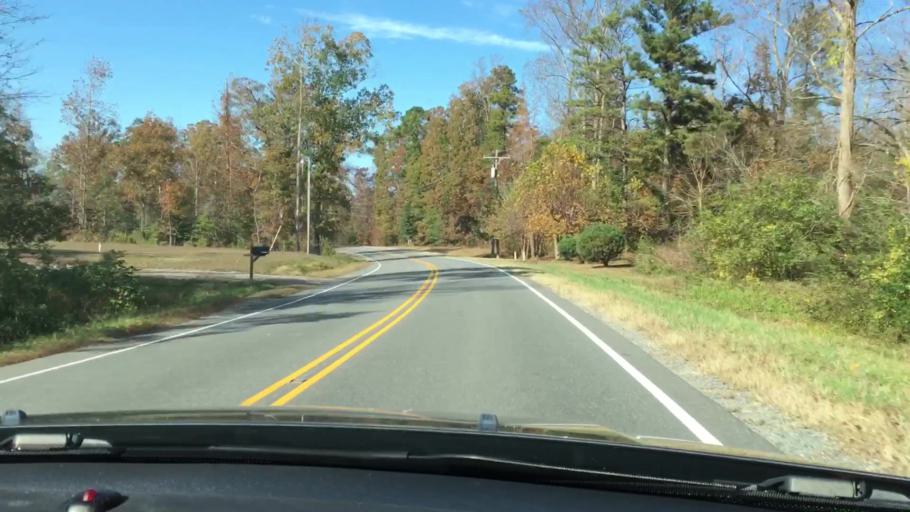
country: US
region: Virginia
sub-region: King and Queen County
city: King and Queen Court House
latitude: 37.6121
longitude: -76.9122
